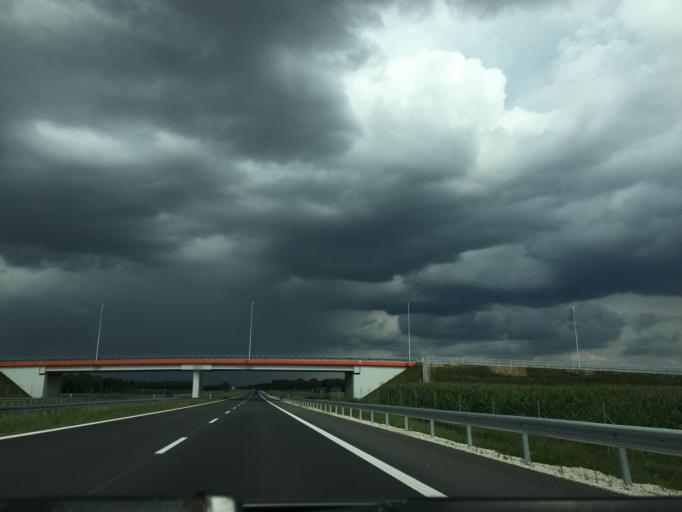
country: PL
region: Masovian Voivodeship
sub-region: Powiat szydlowiecki
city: Jastrzab
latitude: 51.2785
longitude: 20.9592
